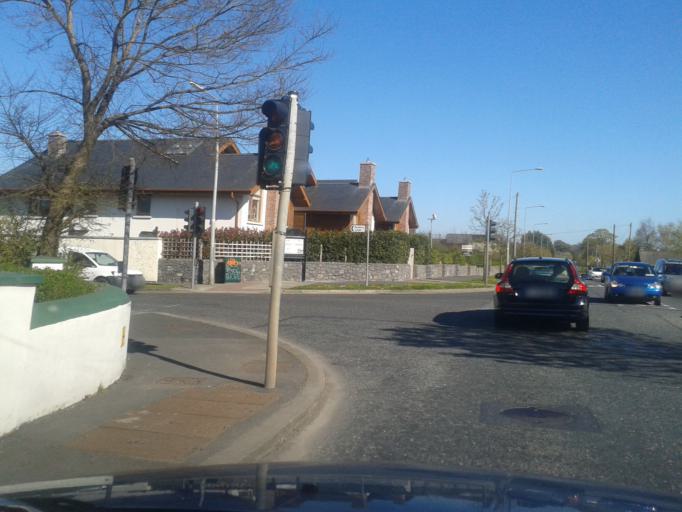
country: IE
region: Leinster
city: Kinsealy-Drinan
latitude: 53.4503
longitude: -6.1862
